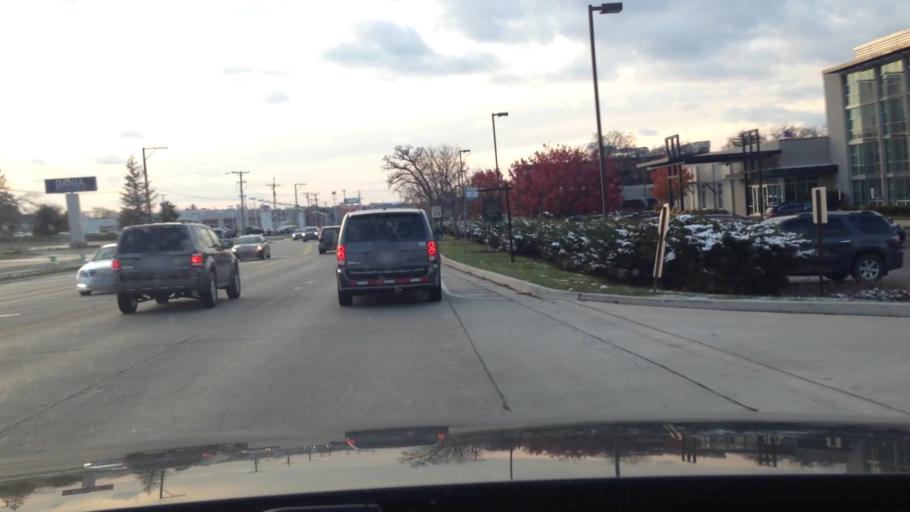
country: US
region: Illinois
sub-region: DuPage County
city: Lombard
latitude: 41.8599
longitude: -88.0274
